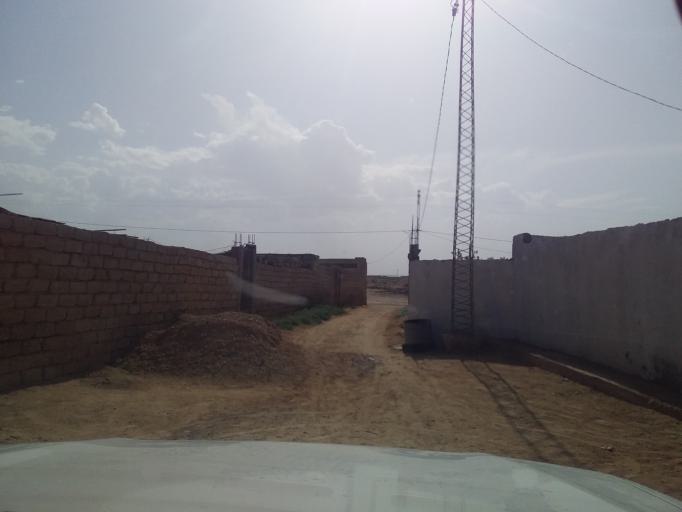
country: TN
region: Qabis
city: Gabes
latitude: 33.6413
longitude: 10.2959
